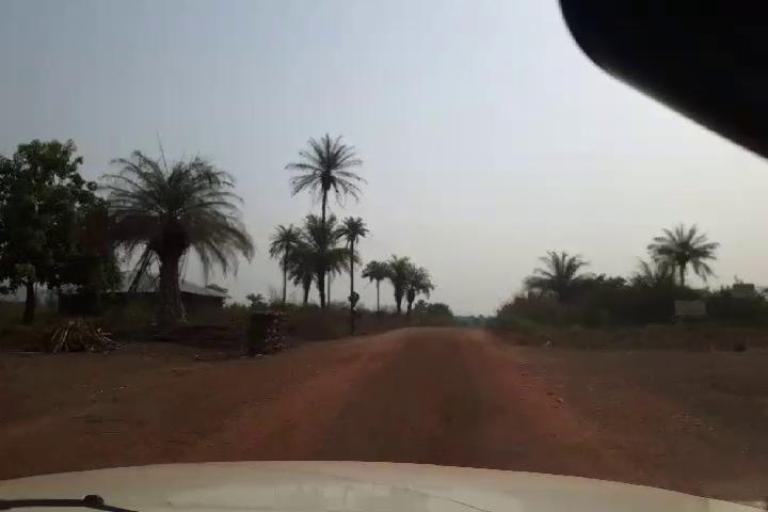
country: SL
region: Northern Province
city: Masingbi
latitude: 8.8268
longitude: -11.8531
